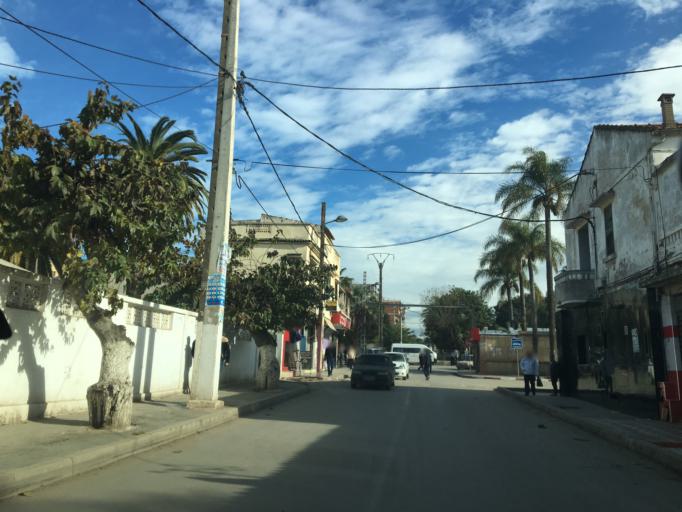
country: DZ
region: Alger
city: Ain Taya
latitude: 36.7907
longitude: 3.2492
